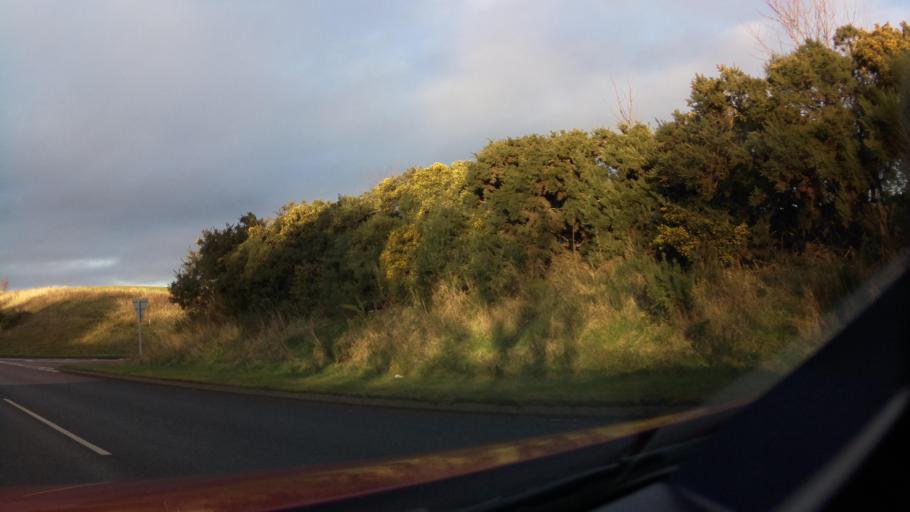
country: GB
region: Scotland
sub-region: Fife
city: Tayport
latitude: 56.4979
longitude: -2.8038
